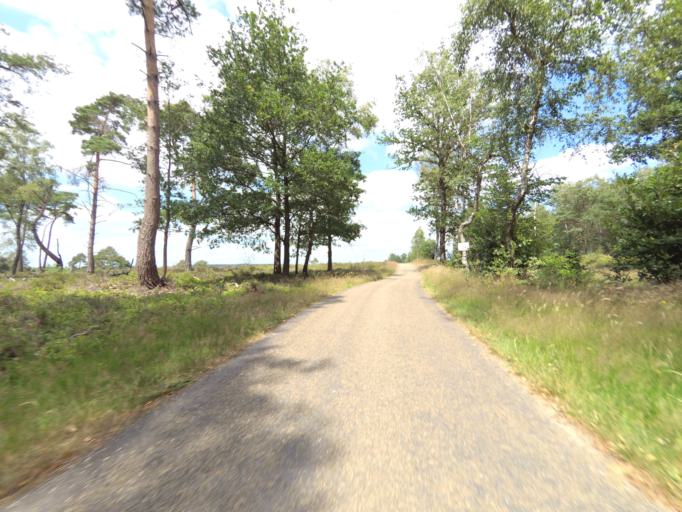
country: NL
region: Overijssel
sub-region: Gemeente Hof van Twente
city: Markelo
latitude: 52.3350
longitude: 6.4506
